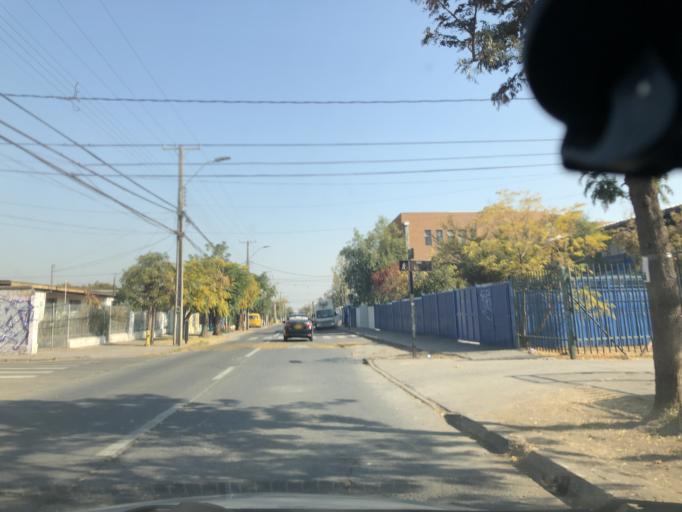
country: CL
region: Santiago Metropolitan
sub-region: Provincia de Cordillera
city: Puente Alto
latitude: -33.6034
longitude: -70.5698
